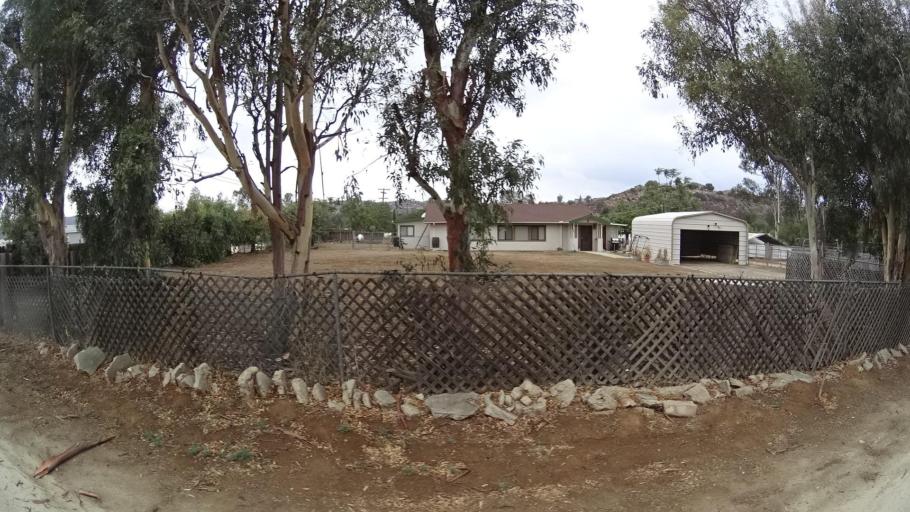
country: US
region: California
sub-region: San Diego County
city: Ramona
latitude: 33.0437
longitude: -116.8946
